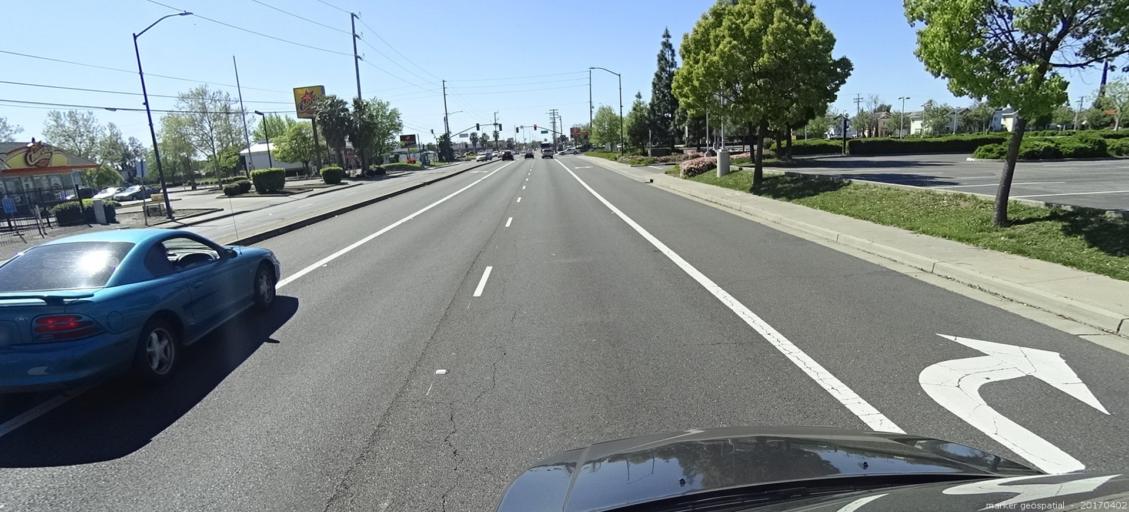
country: US
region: California
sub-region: Sacramento County
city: Parkway
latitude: 38.4959
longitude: -121.4723
